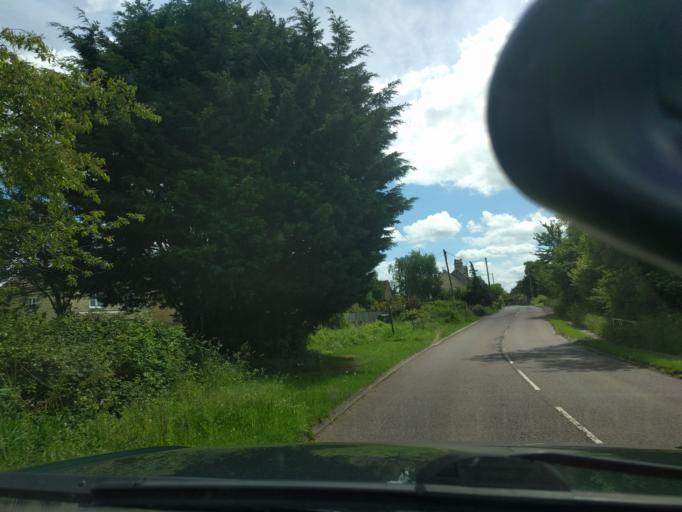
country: GB
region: England
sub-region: Wiltshire
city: Corsham
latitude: 51.4223
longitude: -2.1800
